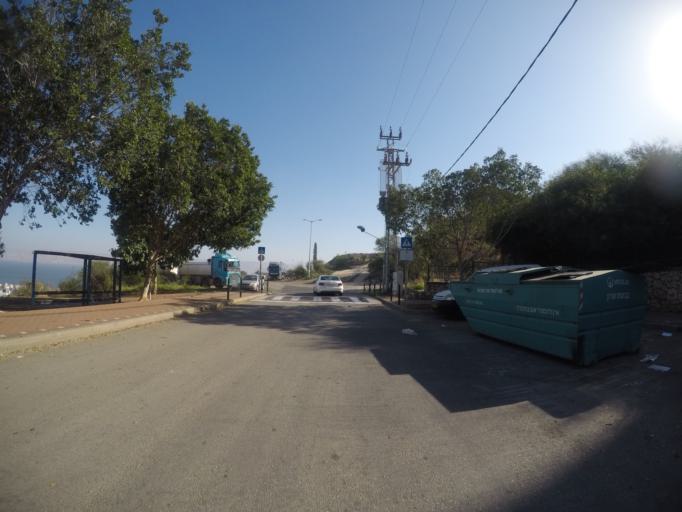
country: IL
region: Northern District
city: Tiberias
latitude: 32.7896
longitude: 35.5272
